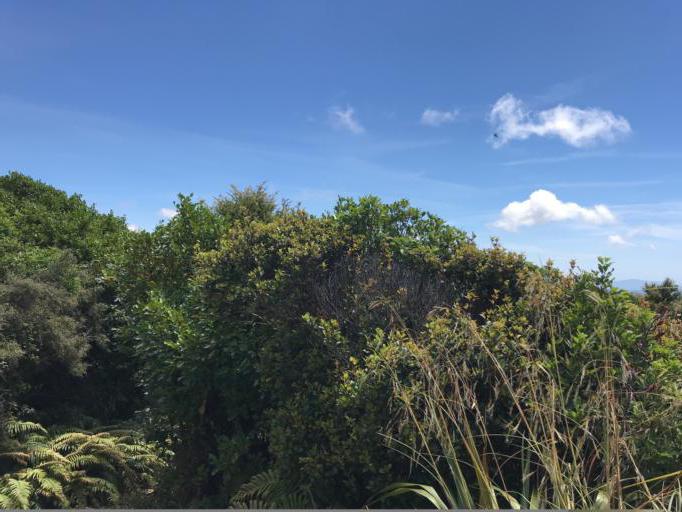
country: NZ
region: Wellington
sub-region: Kapiti Coast District
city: Otaki
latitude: -40.9100
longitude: 175.2604
